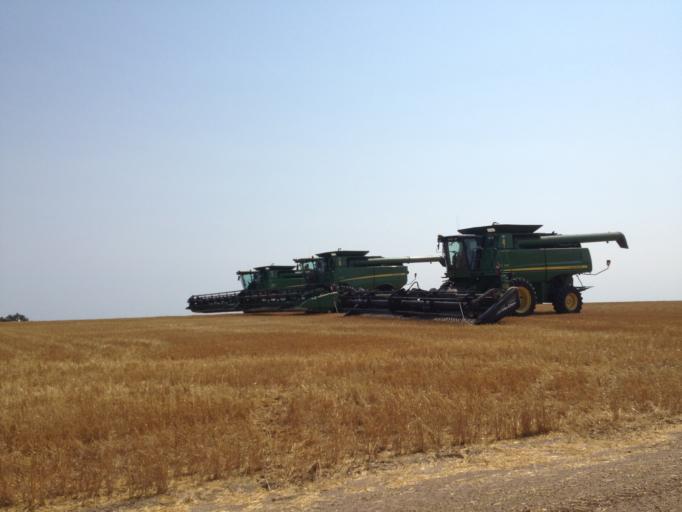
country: US
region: North Dakota
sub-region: Adams County
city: Hettinger
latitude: 45.9007
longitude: -102.9425
